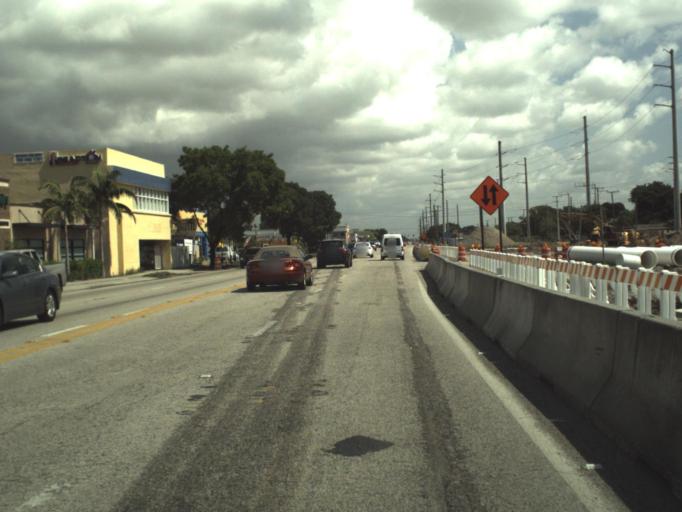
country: US
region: Florida
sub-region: Broward County
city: Pembroke Pines
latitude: 26.0115
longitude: -80.2076
